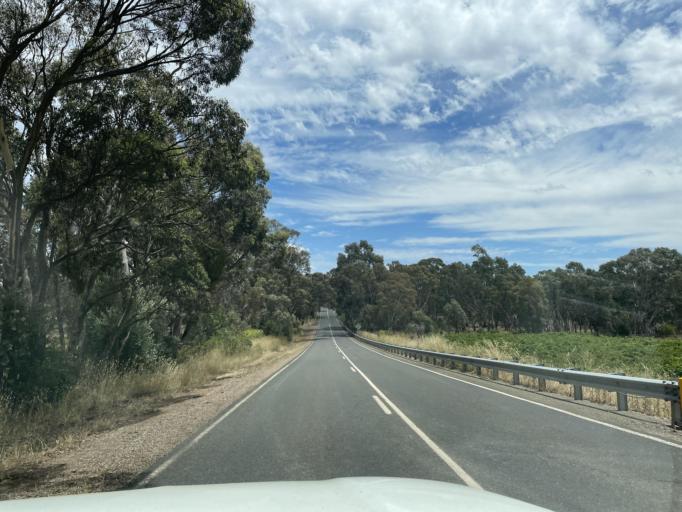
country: AU
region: South Australia
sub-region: Clare and Gilbert Valleys
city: Clare
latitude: -33.8977
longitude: 138.6834
